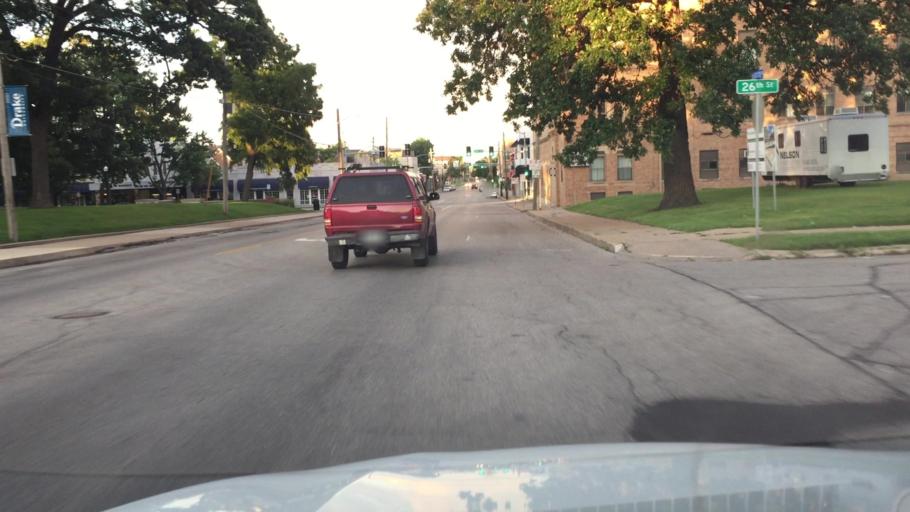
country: US
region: Iowa
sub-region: Polk County
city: Des Moines
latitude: 41.6004
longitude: -93.6523
